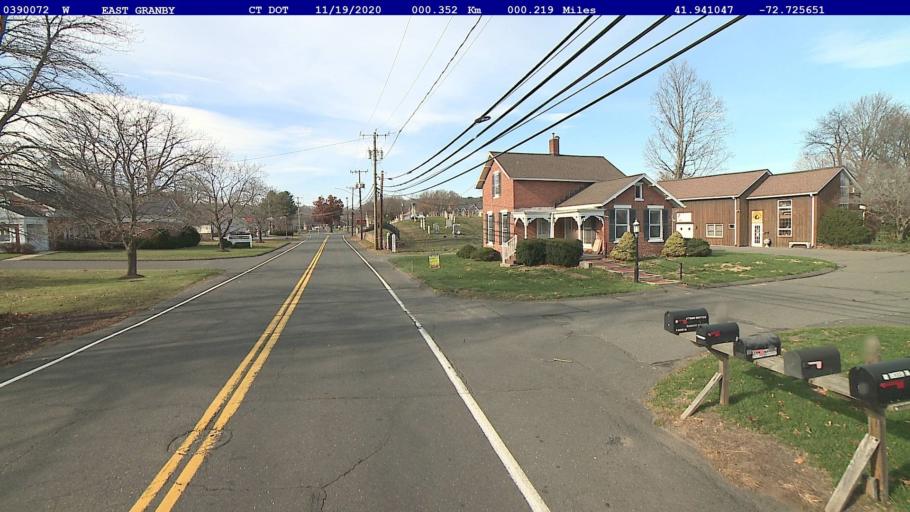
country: US
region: Connecticut
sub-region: Hartford County
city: Tariffville
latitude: 41.9411
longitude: -72.7257
